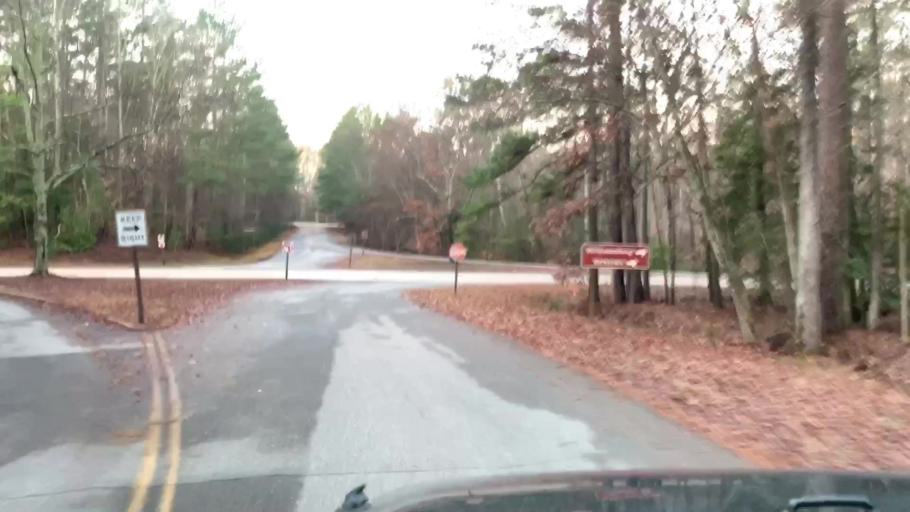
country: US
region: Virginia
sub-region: City of Williamsburg
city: Williamsburg
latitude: 37.2496
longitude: -76.7001
